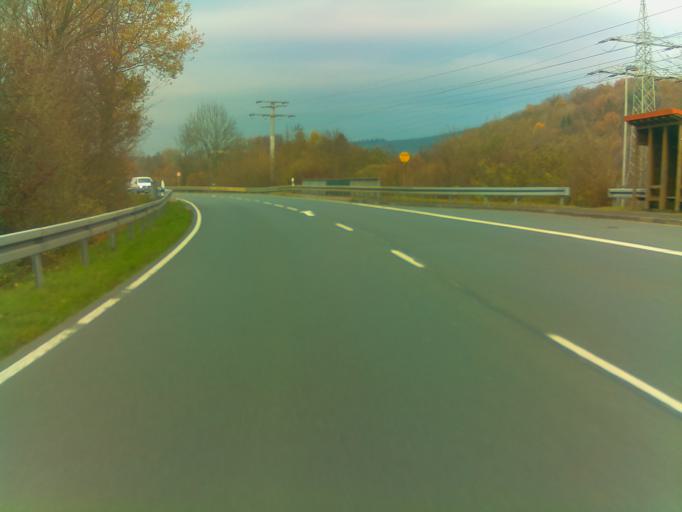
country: DE
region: Bavaria
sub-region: Regierungsbezirk Unterfranken
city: Weilbach
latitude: 49.6909
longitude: 9.2235
